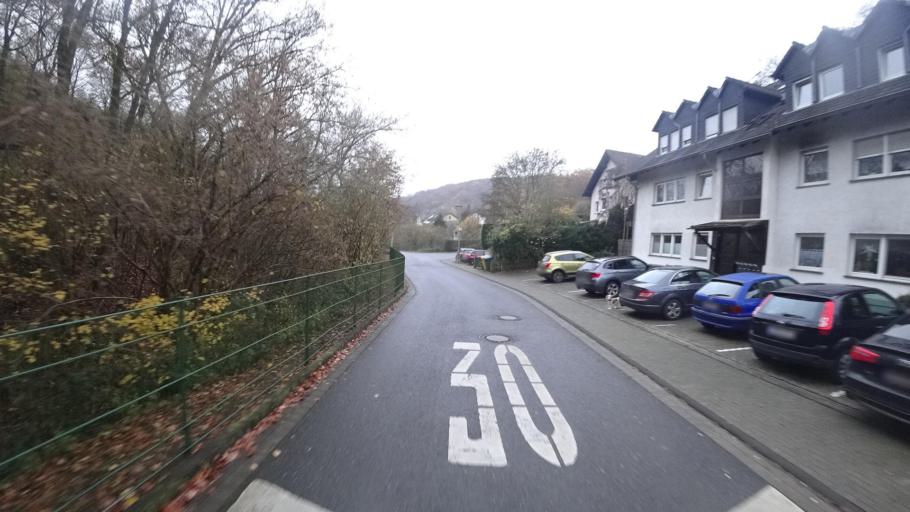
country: DE
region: Rheinland-Pfalz
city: Remagen
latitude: 50.5565
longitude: 7.1848
